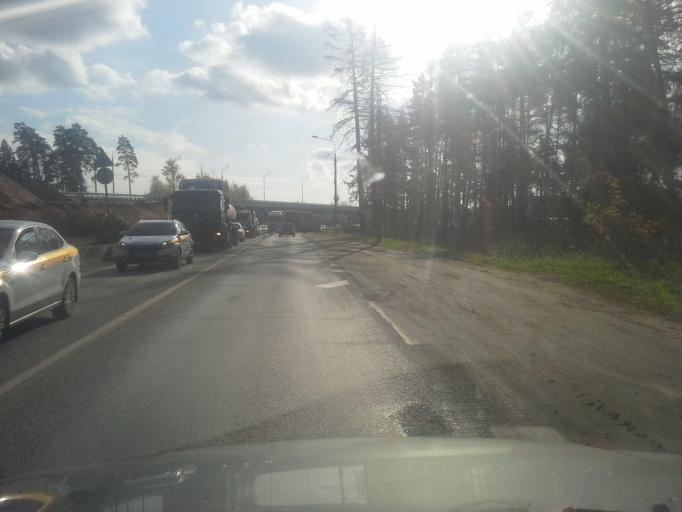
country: RU
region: Moskovskaya
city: Zvenigorod
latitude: 55.7028
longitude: 36.8801
